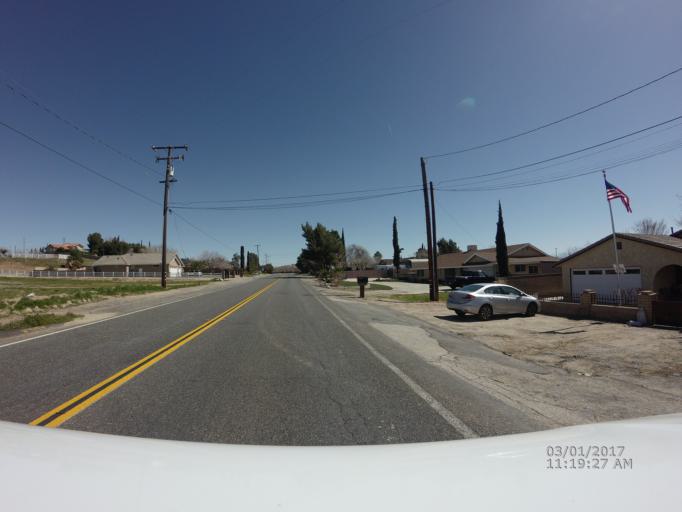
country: US
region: California
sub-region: Los Angeles County
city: Quartz Hill
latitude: 34.6439
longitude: -118.2118
